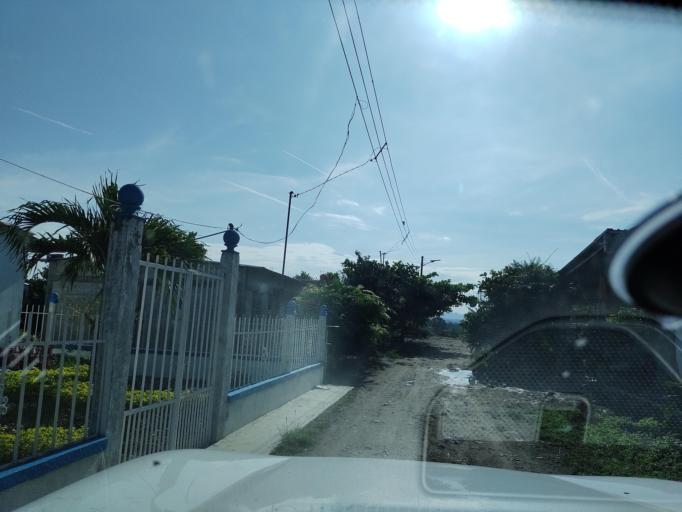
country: MX
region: Veracruz
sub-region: Martinez de la Torre
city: El Progreso
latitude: 20.1141
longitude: -96.9875
